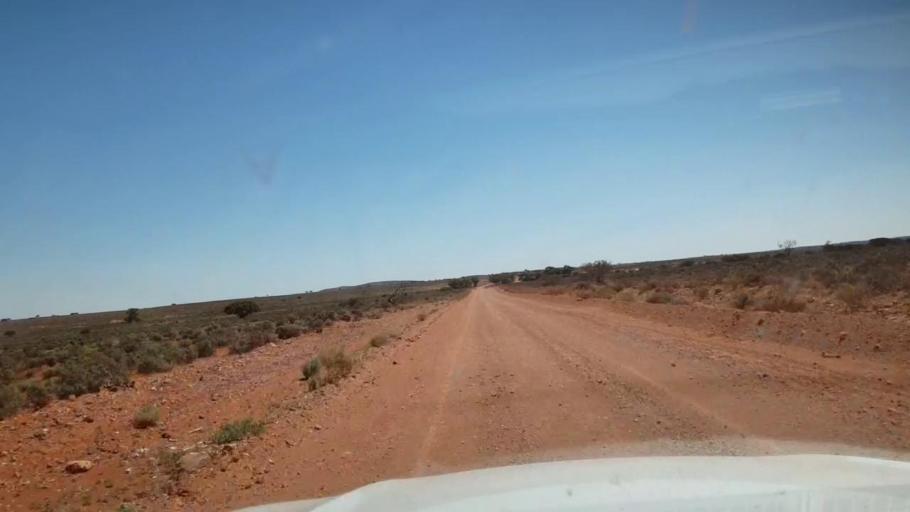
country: AU
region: South Australia
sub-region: Whyalla
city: Whyalla
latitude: -32.6834
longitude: 137.0957
